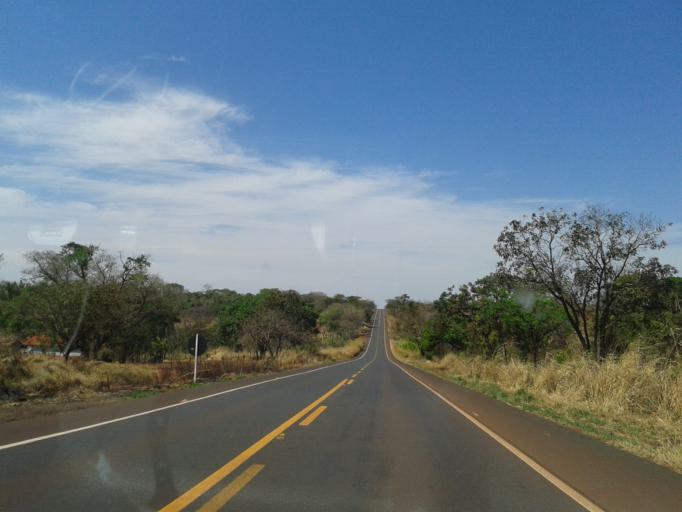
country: BR
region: Minas Gerais
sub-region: Santa Vitoria
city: Santa Vitoria
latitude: -18.9136
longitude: -49.8875
